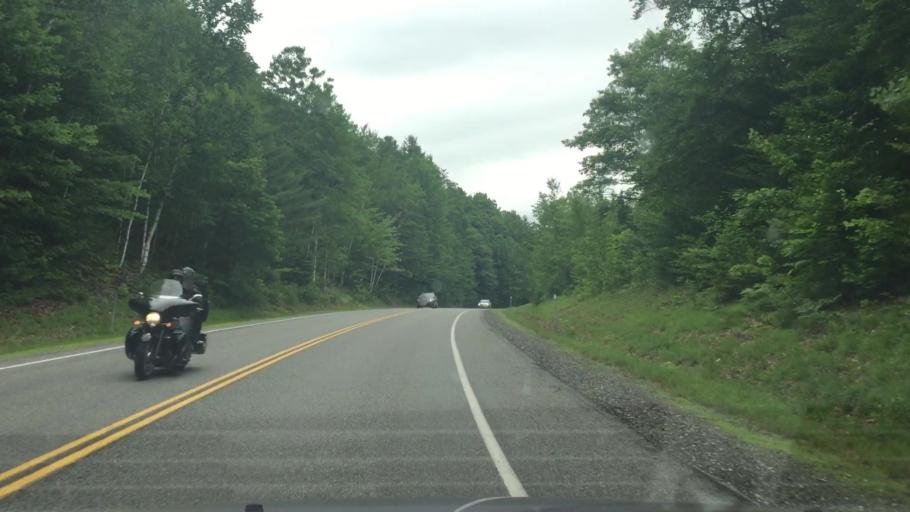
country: US
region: New Hampshire
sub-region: Carroll County
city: North Conway
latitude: 44.0959
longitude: -71.3549
